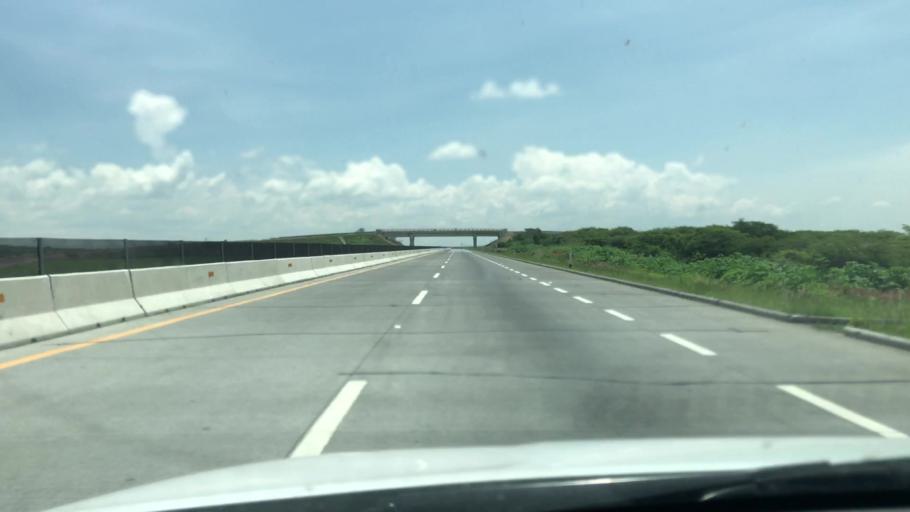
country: MX
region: Jalisco
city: Degollado
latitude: 20.3848
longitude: -102.1156
